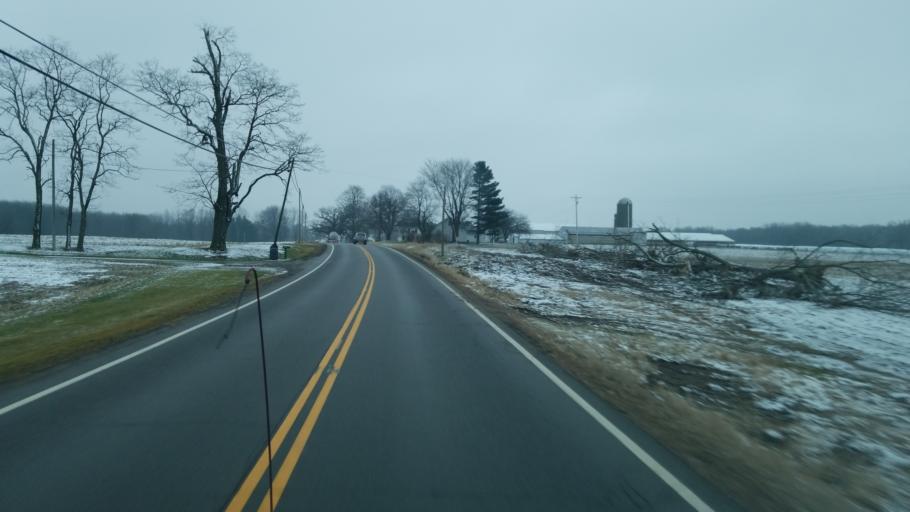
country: US
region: Ohio
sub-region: Wayne County
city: Shreve
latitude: 40.7665
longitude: -82.0435
